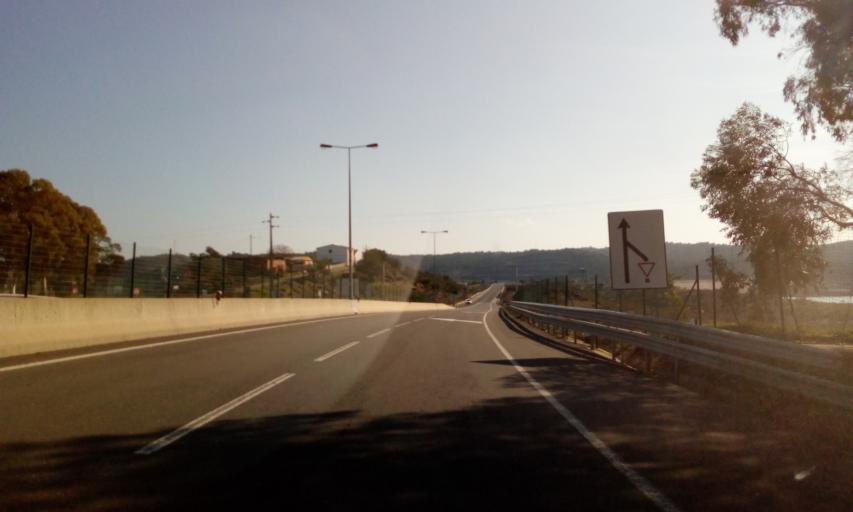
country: PT
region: Faro
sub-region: Castro Marim
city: Castro Marim
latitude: 37.3342
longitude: -7.4907
